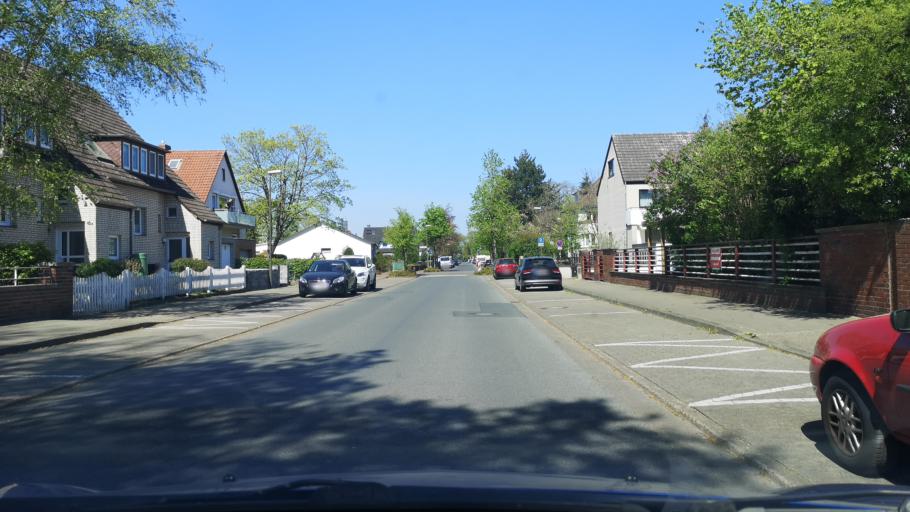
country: DE
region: Lower Saxony
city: Langenhagen
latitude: 52.4499
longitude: 9.7503
